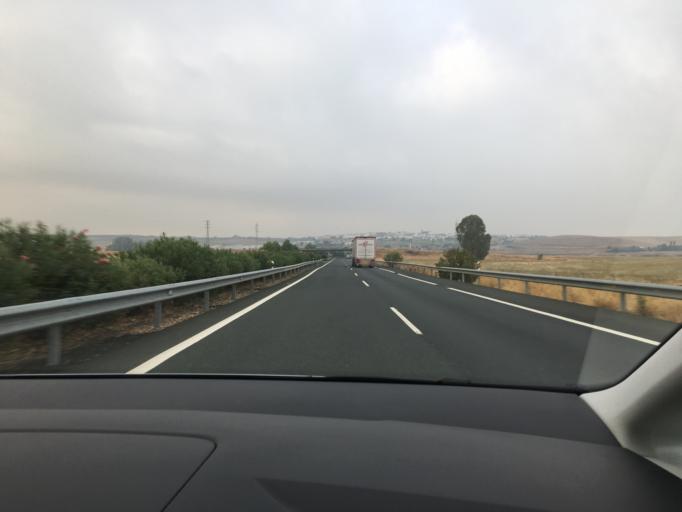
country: ES
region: Andalusia
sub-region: Province of Cordoba
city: La Carlota
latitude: 37.6891
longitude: -4.9226
